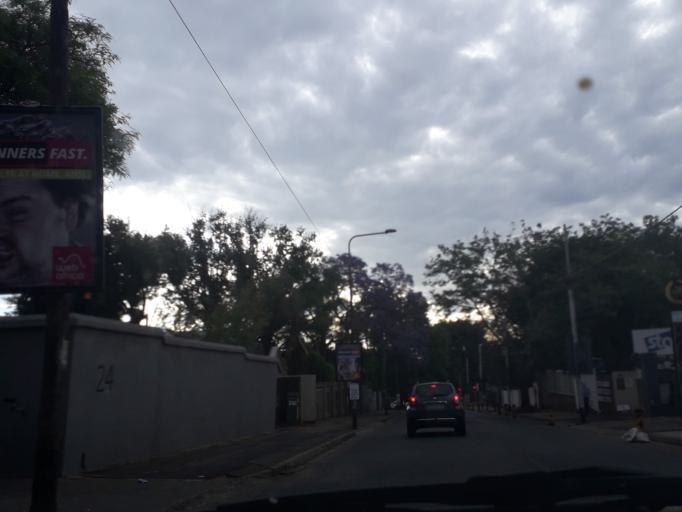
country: ZA
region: Gauteng
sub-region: City of Johannesburg Metropolitan Municipality
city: Johannesburg
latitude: -26.1447
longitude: 28.0265
